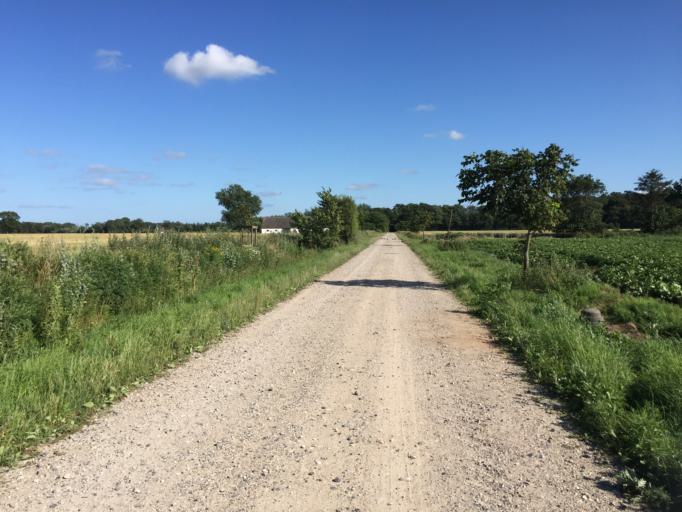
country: DK
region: South Denmark
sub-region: Kerteminde Kommune
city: Langeskov
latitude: 55.3710
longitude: 10.5450
